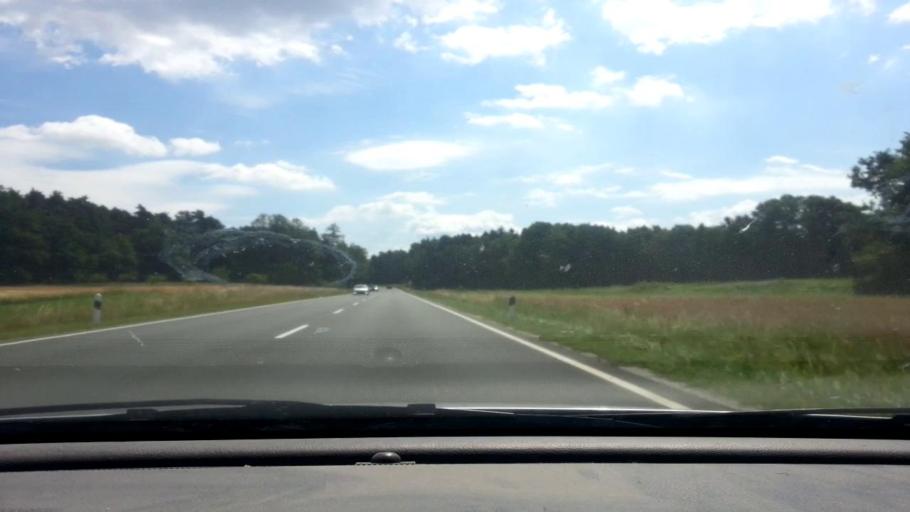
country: DE
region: Bavaria
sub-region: Upper Palatinate
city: Immenreuth
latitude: 49.8716
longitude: 11.8424
